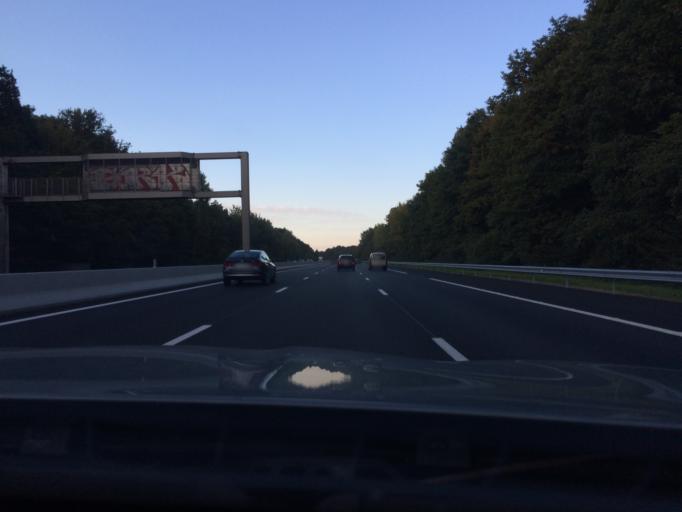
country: FR
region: Ile-de-France
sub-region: Departement de l'Essonne
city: Soisy-sur-Ecole
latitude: 48.4972
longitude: 2.5130
